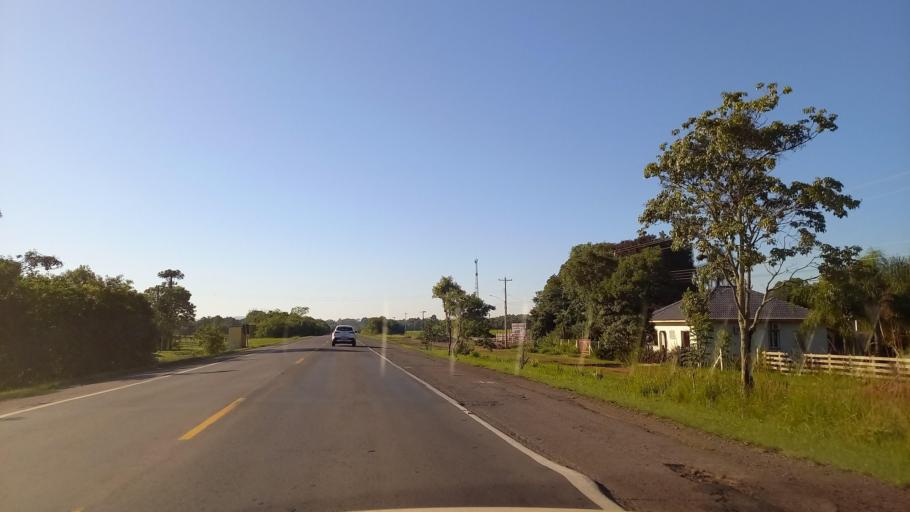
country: BR
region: Rio Grande do Sul
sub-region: Venancio Aires
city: Venancio Aires
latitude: -29.6658
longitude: -52.0513
